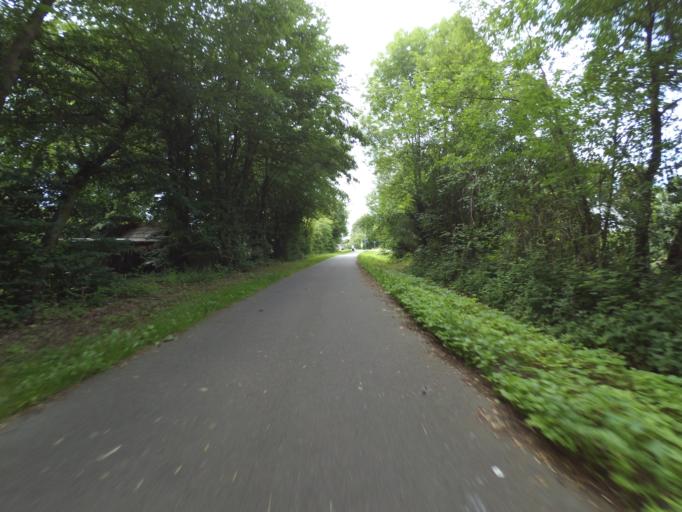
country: DE
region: North Rhine-Westphalia
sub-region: Regierungsbezirk Koln
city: Roetgen
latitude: 50.6397
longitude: 6.1901
